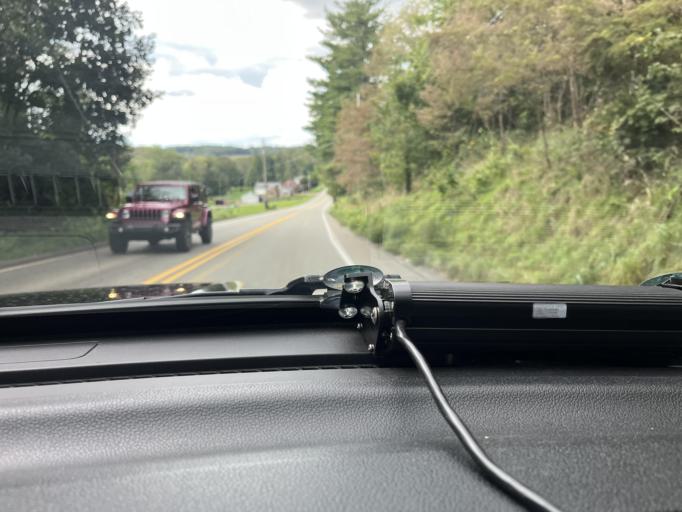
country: US
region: Pennsylvania
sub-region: Fayette County
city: South Uniontown
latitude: 39.9090
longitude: -79.7593
